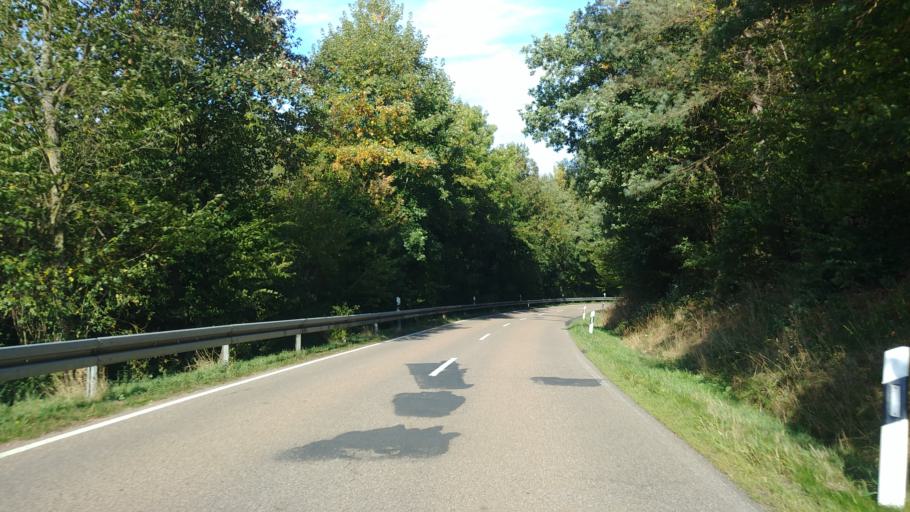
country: DE
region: Hesse
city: Taunusstein
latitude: 50.2056
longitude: 8.1269
